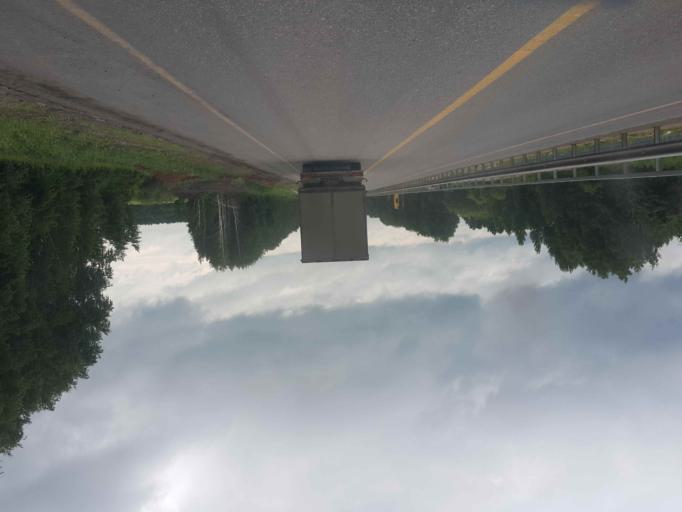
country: RU
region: Tambov
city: Selezni
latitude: 52.8001
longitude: 40.9856
